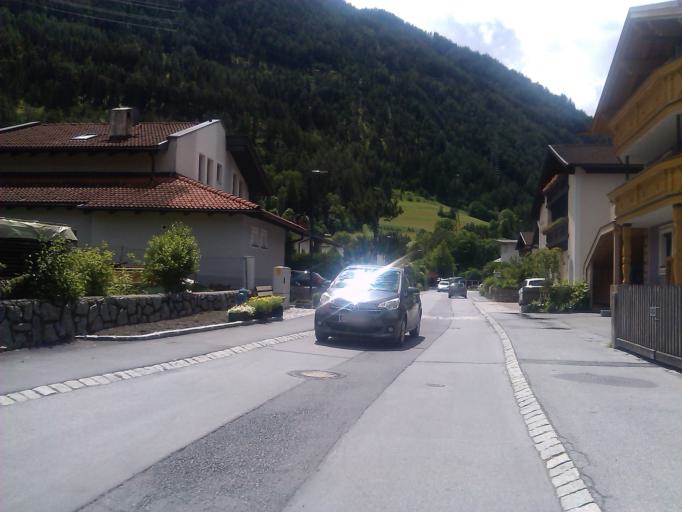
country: AT
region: Tyrol
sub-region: Politischer Bezirk Landeck
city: Prutz
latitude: 47.0736
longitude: 10.6655
